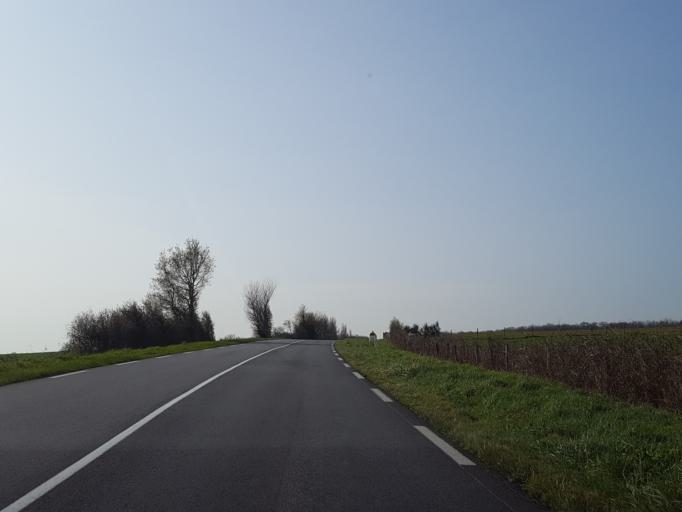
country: FR
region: Pays de la Loire
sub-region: Departement de la Vendee
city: Rocheserviere
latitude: 46.9091
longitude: -1.5039
